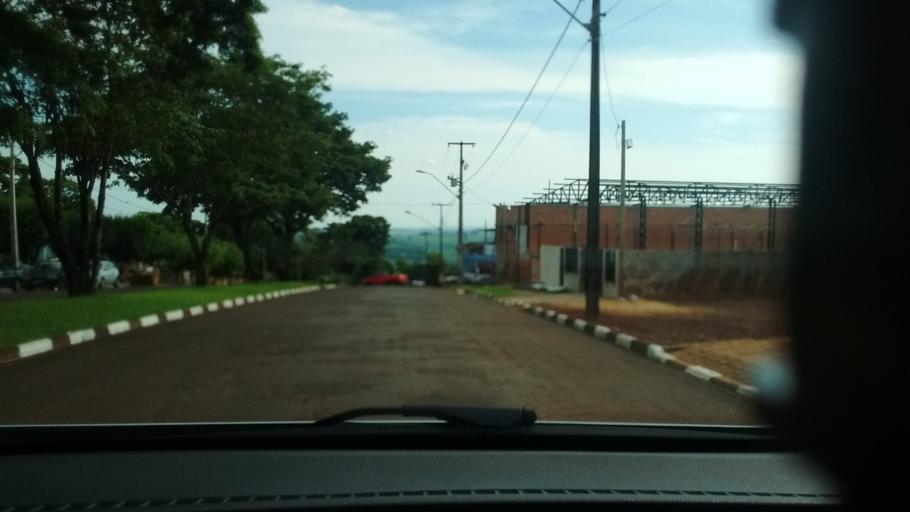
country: BR
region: Parana
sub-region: Corbelia
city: Corbelia
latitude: -24.5543
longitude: -52.9890
